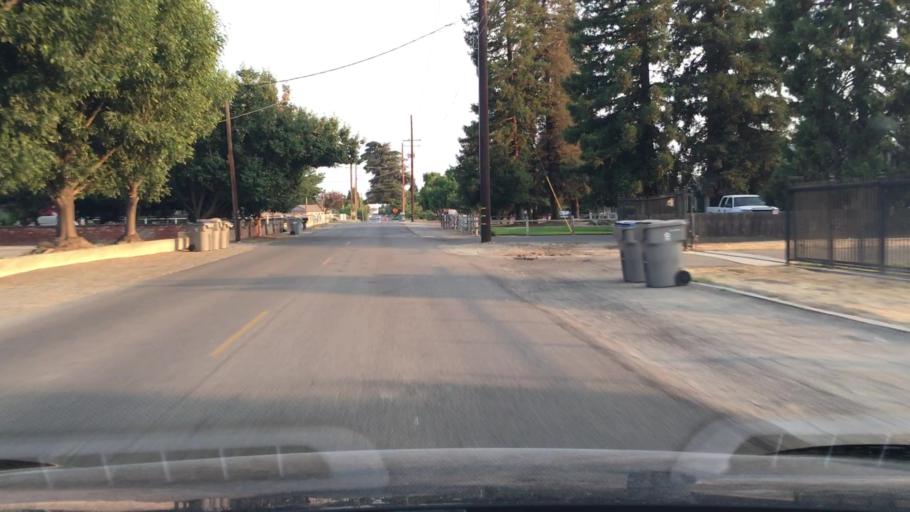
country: US
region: California
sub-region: Fresno County
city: Clovis
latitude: 36.8554
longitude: -119.6931
